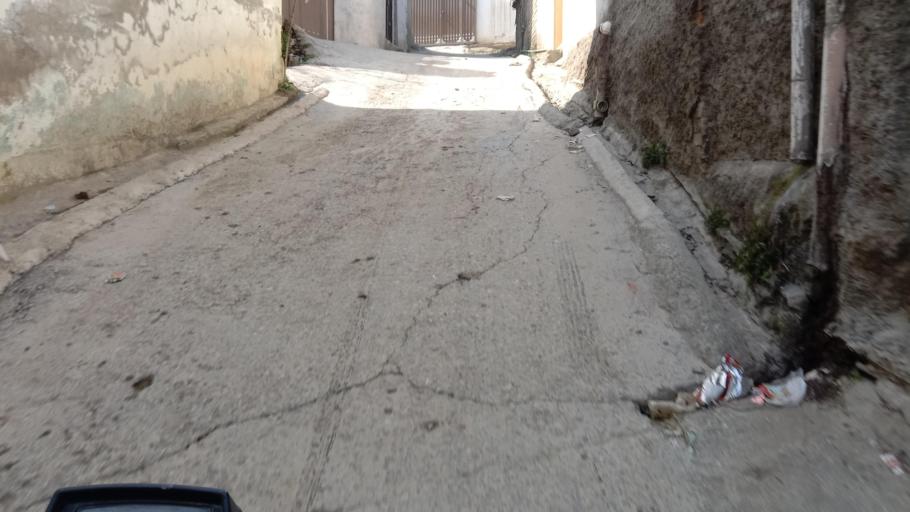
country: PK
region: Khyber Pakhtunkhwa
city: Abbottabad
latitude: 34.1772
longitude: 73.2113
